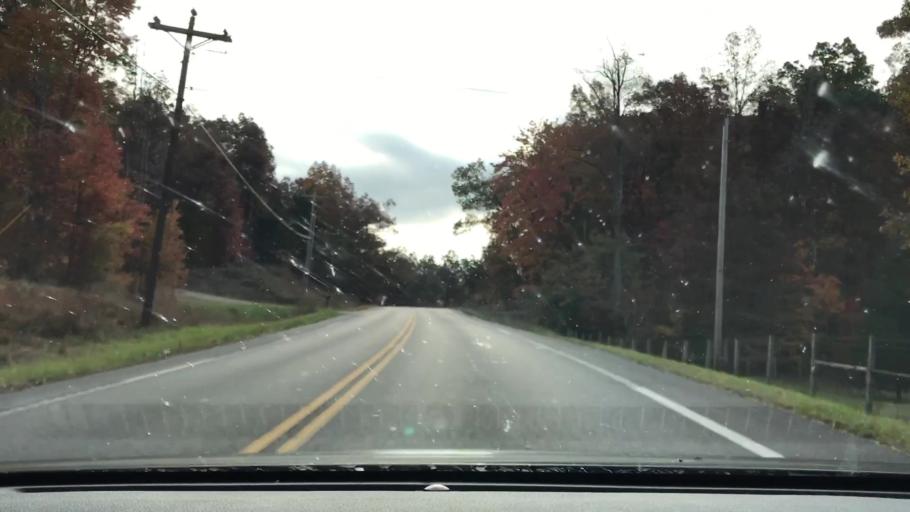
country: US
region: Tennessee
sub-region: Putnam County
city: Monterey
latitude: 36.1287
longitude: -85.2034
